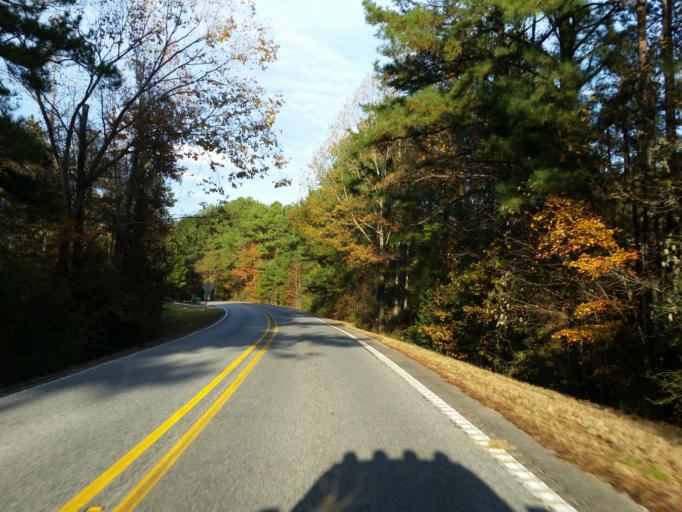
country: US
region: Mississippi
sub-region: Clarke County
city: Stonewall
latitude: 32.2007
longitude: -88.7987
